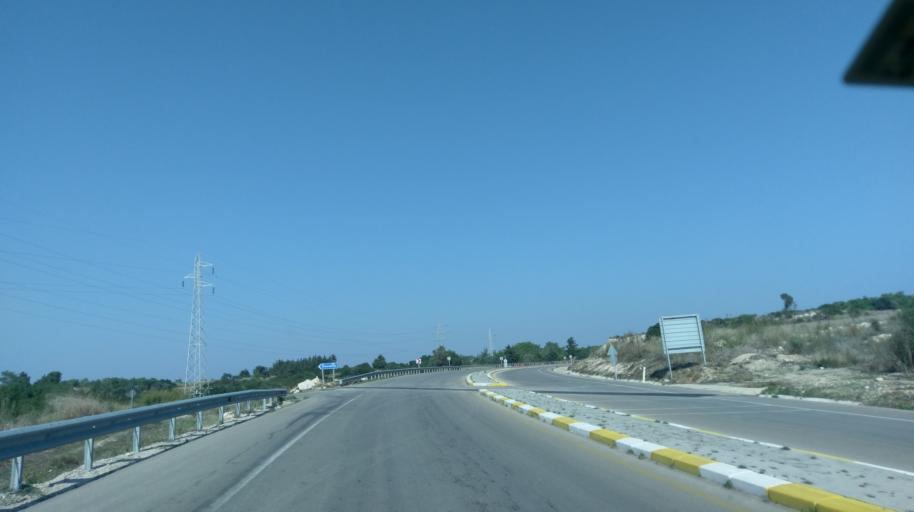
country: CY
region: Ammochostos
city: Leonarisso
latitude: 35.4787
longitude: 34.1425
